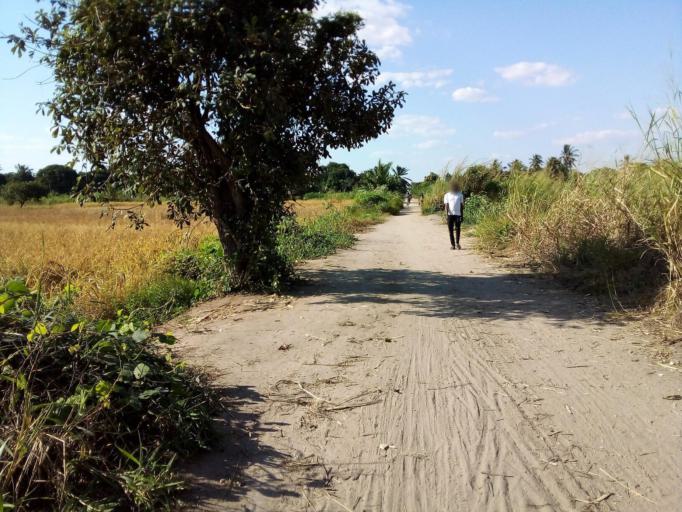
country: MZ
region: Zambezia
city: Quelimane
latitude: -17.5947
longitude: 36.8311
